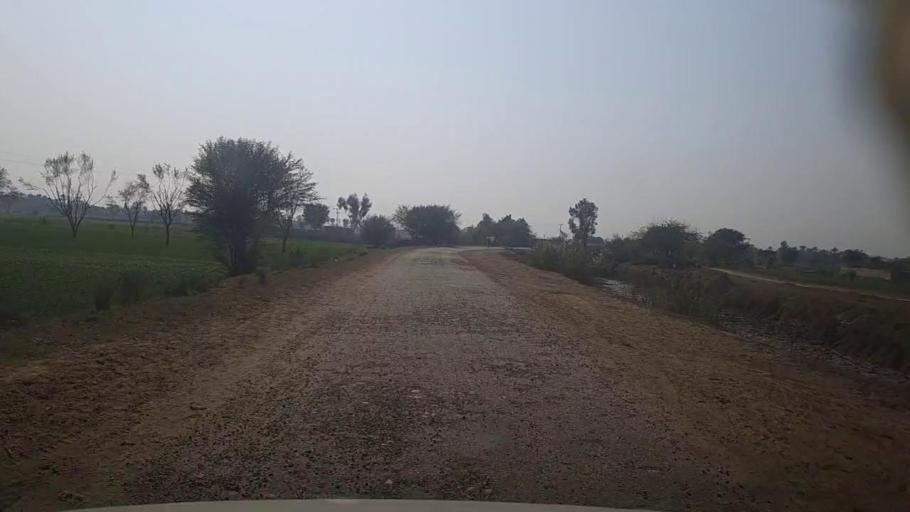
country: PK
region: Sindh
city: Kot Diji
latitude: 27.3669
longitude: 68.7479
